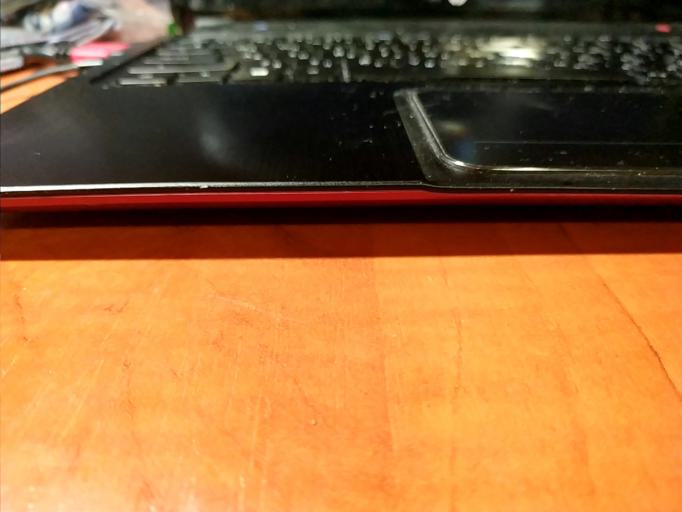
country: RU
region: Tverskaya
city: Ves'yegonsk
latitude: 58.7572
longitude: 37.5437
